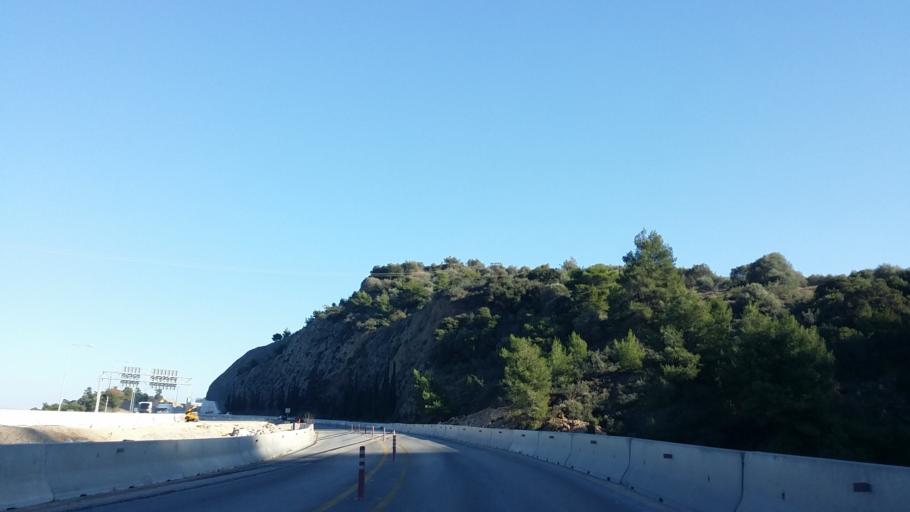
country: GR
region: West Greece
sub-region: Nomos Achaias
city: Akrata
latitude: 38.1744
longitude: 22.2451
